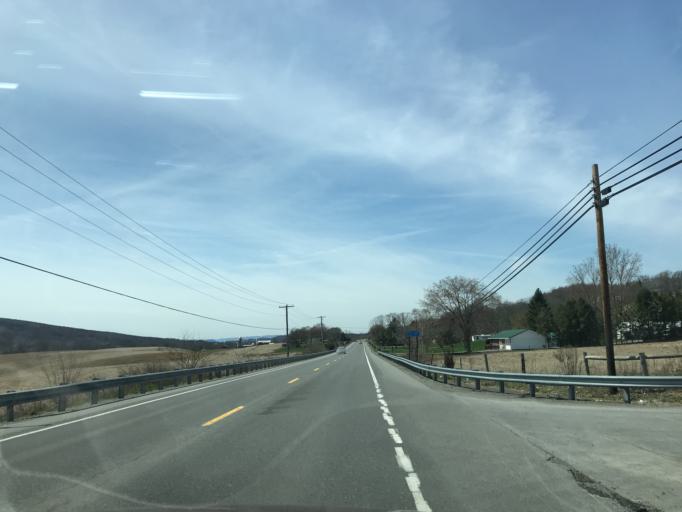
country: US
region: Pennsylvania
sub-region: Snyder County
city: Selinsgrove
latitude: 40.8067
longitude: -76.9390
